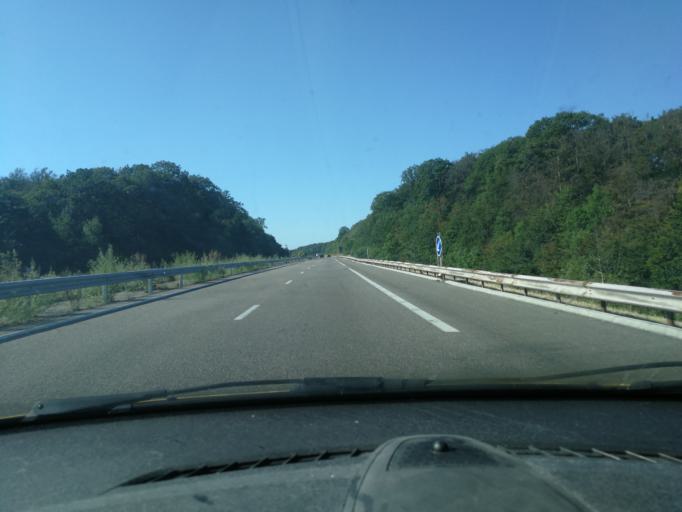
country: FR
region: Alsace
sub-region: Departement du Bas-Rhin
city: Sarrewerden
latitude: 48.8885
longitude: 7.1229
